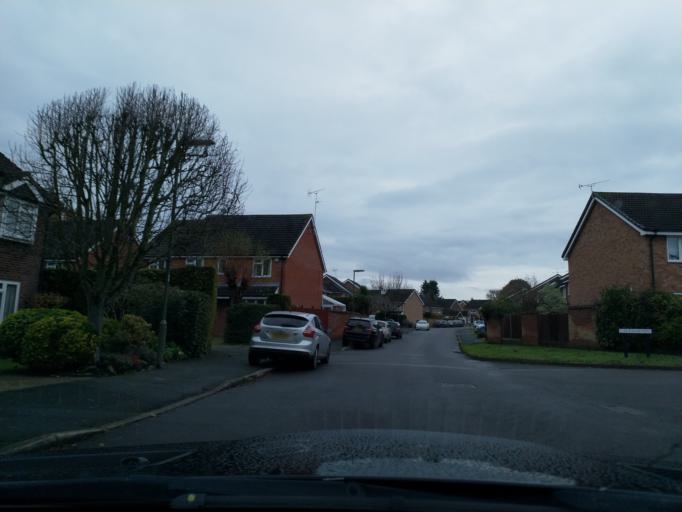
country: GB
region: England
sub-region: Surrey
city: Frimley
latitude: 51.3111
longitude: -0.7257
